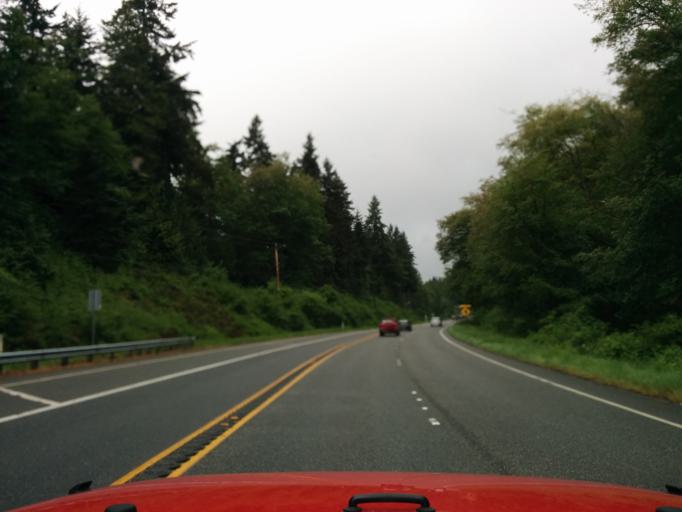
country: US
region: Washington
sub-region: Island County
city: Langley
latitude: 47.9789
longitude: -122.3775
